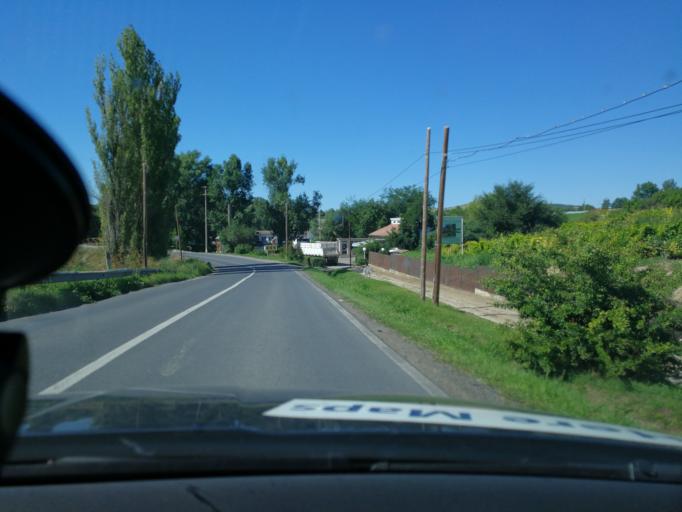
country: RO
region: Tulcea
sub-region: Oras Macin
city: Macin
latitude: 45.2415
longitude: 28.1477
